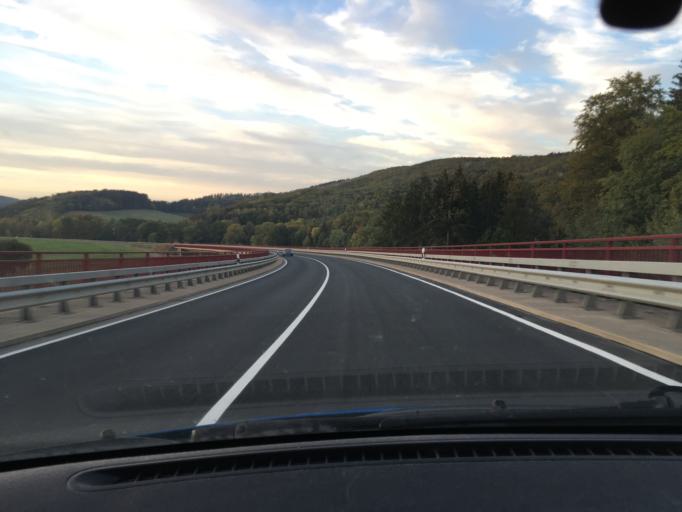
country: DE
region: Lower Saxony
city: Hardegsen
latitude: 51.6538
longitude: 9.7644
